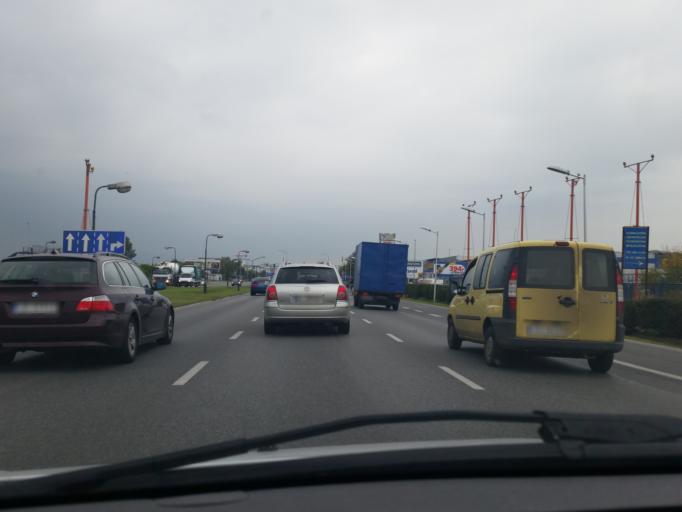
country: PL
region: Masovian Voivodeship
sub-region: Warszawa
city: Wlochy
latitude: 52.1736
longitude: 20.9409
